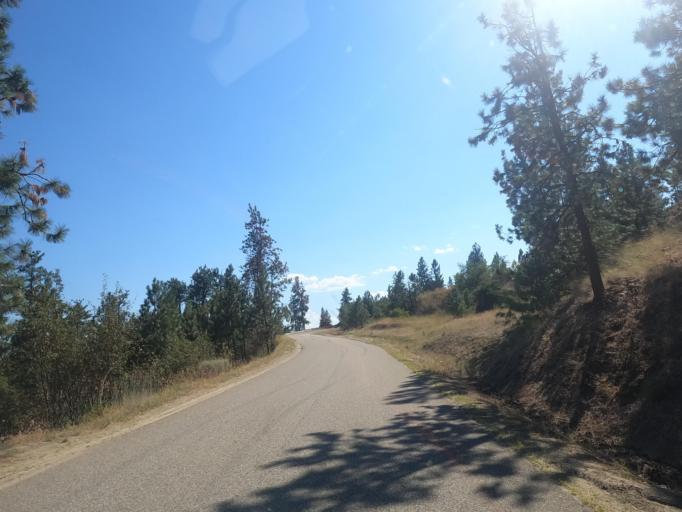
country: CA
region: British Columbia
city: Peachland
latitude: 49.7895
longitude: -119.7097
